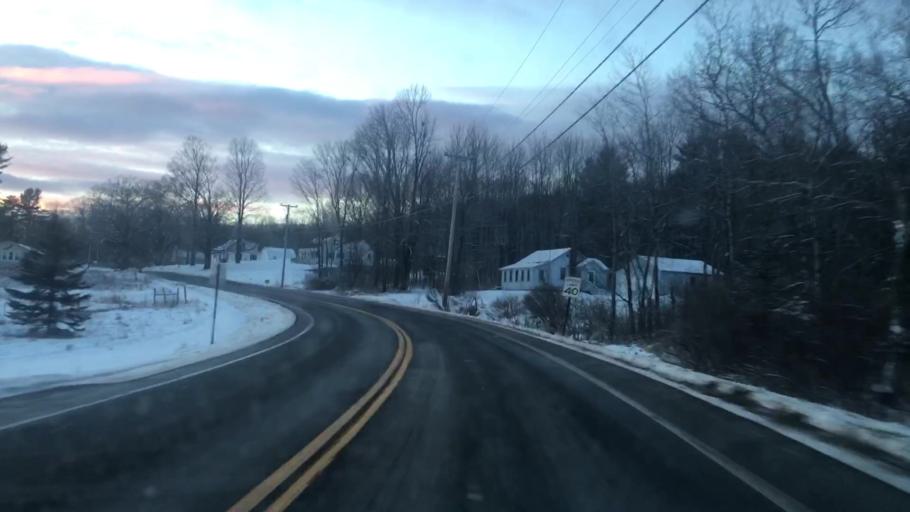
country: US
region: Maine
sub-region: Kennebec County
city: Pittston
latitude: 44.2223
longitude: -69.7332
